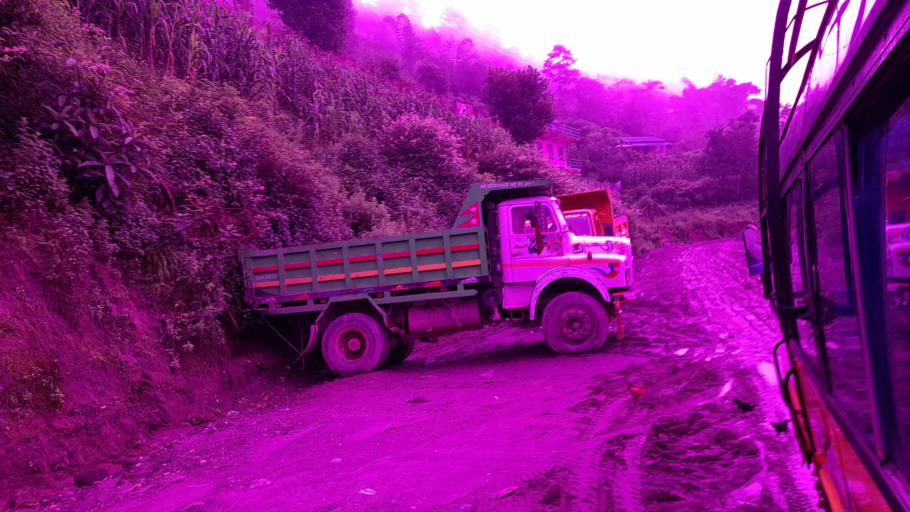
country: NP
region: Central Region
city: Kirtipur
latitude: 27.8180
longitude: 85.2270
